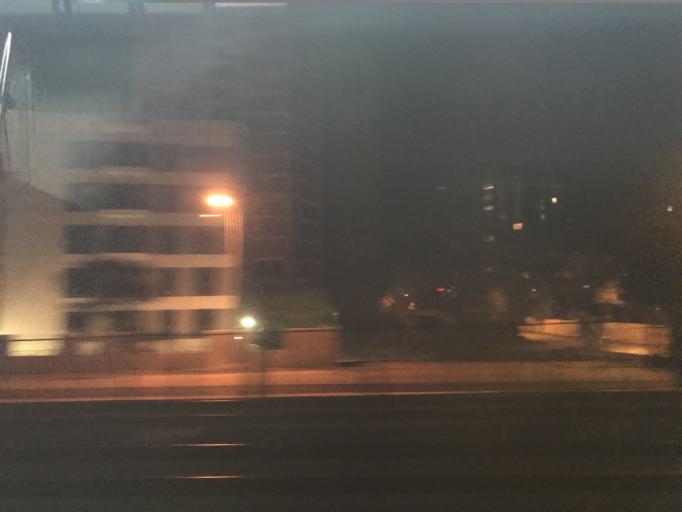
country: TR
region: Istanbul
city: Maltepe
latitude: 40.8947
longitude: 29.1743
